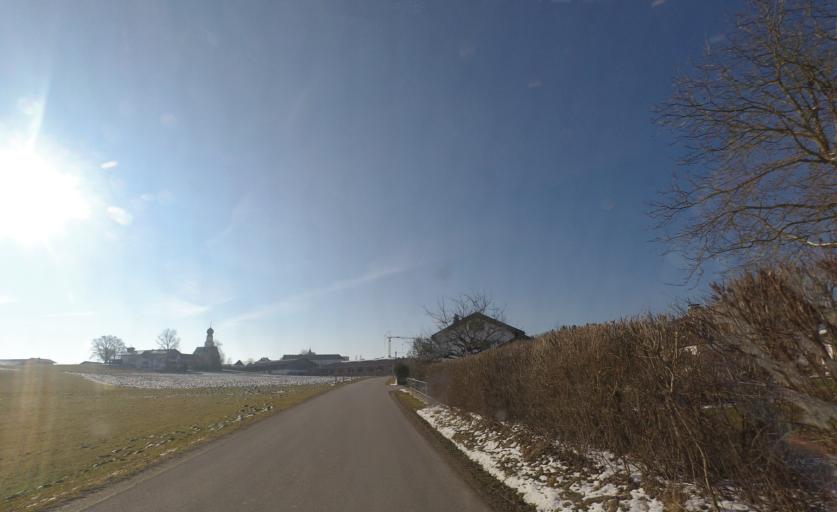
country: DE
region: Bavaria
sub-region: Upper Bavaria
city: Chieming
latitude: 47.9264
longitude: 12.5024
